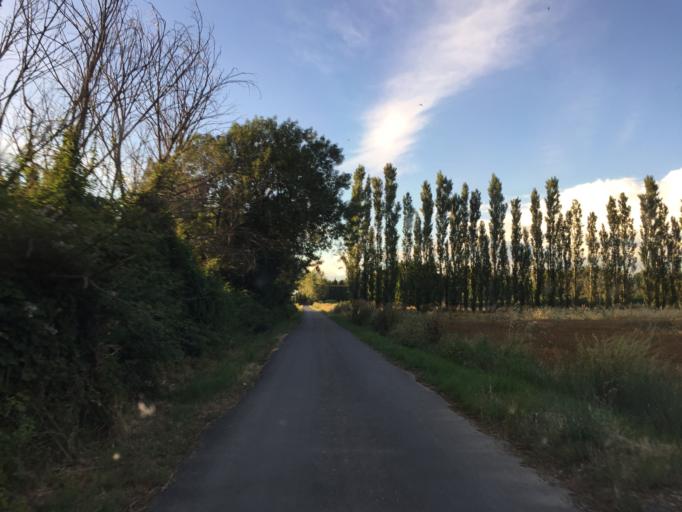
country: FR
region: Provence-Alpes-Cote d'Azur
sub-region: Departement du Vaucluse
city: Orange
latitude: 44.1217
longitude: 4.8459
